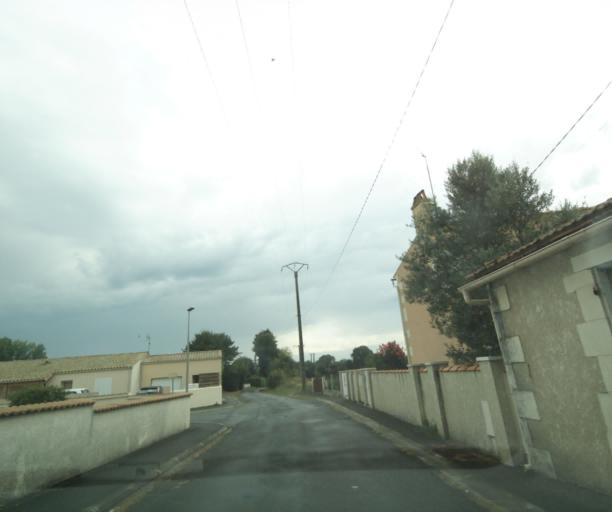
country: FR
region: Poitou-Charentes
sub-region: Departement de la Charente-Maritime
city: Tonnay-Charente
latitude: 45.9492
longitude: -0.9235
